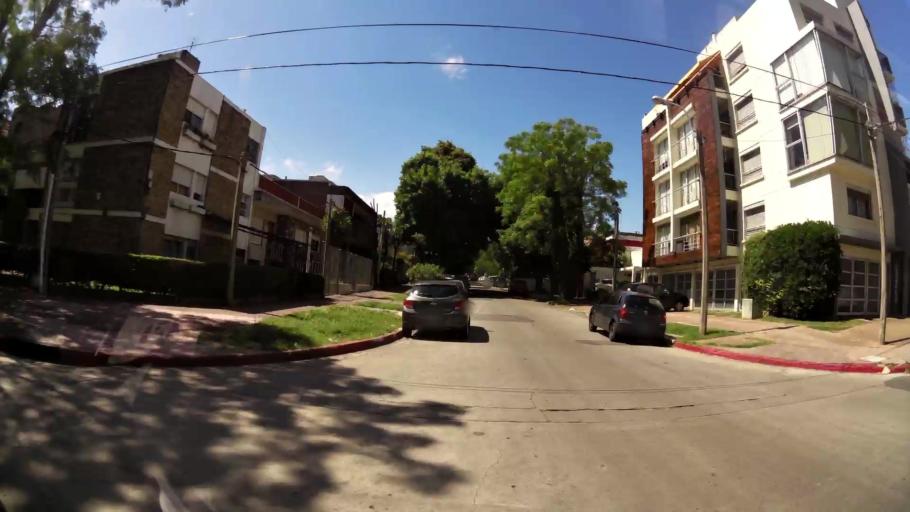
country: UY
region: Montevideo
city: Montevideo
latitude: -34.9020
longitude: -56.1325
